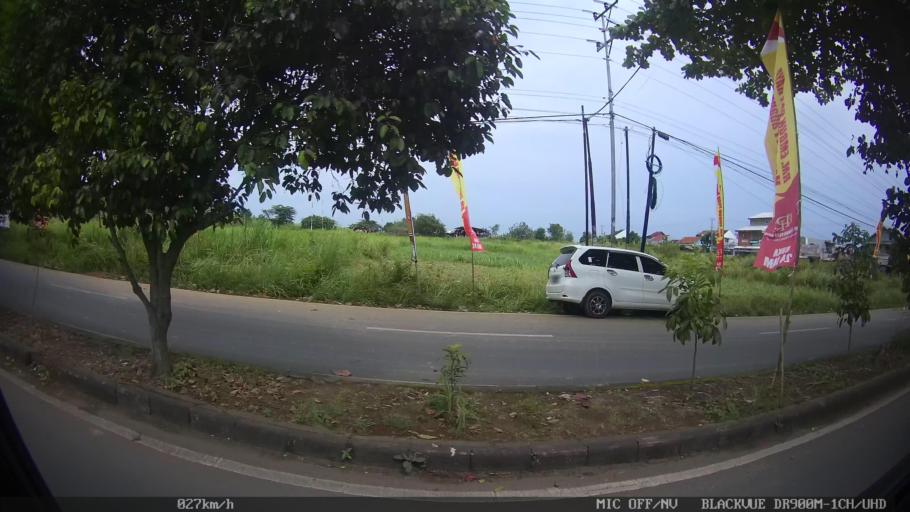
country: ID
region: Lampung
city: Kedaton
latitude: -5.3994
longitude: 105.2032
